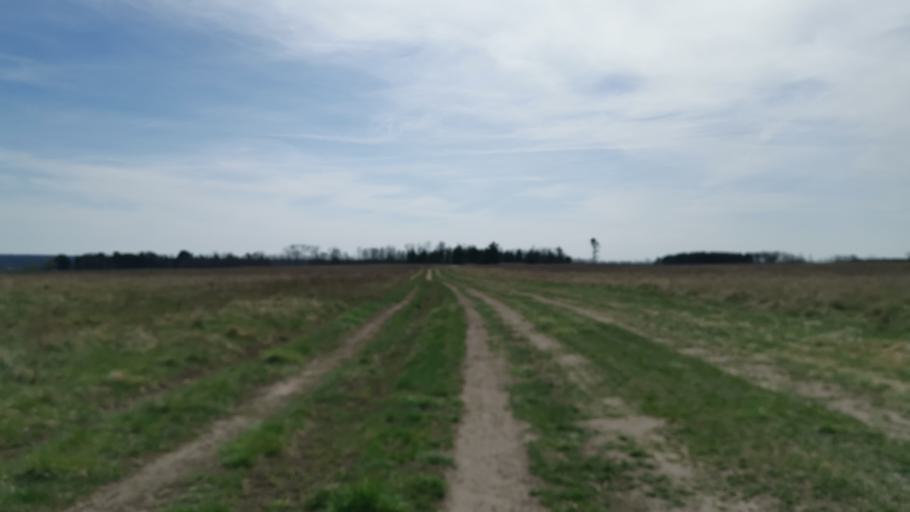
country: SK
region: Trnavsky
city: Gbely
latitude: 48.6685
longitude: 17.1091
